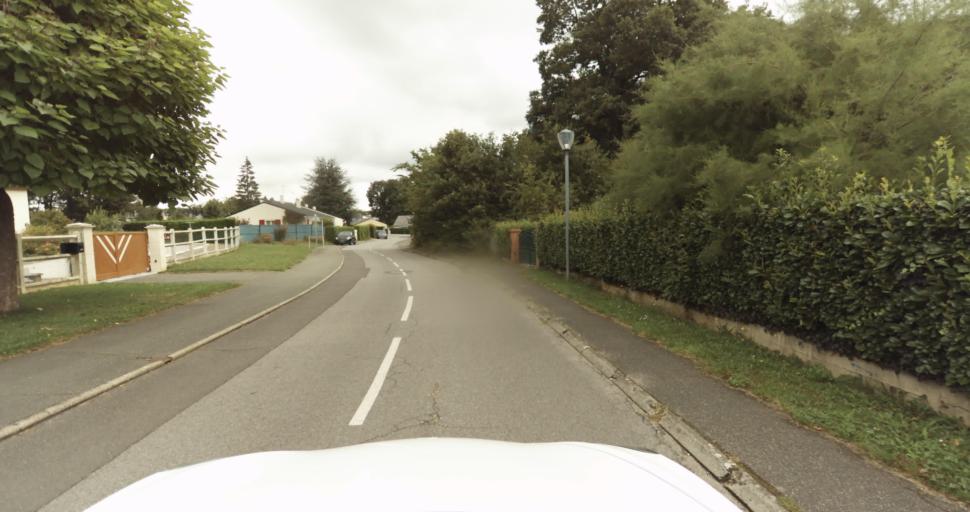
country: FR
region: Haute-Normandie
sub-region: Departement de l'Eure
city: Saint-Sebastien-de-Morsent
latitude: 49.0033
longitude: 1.0934
